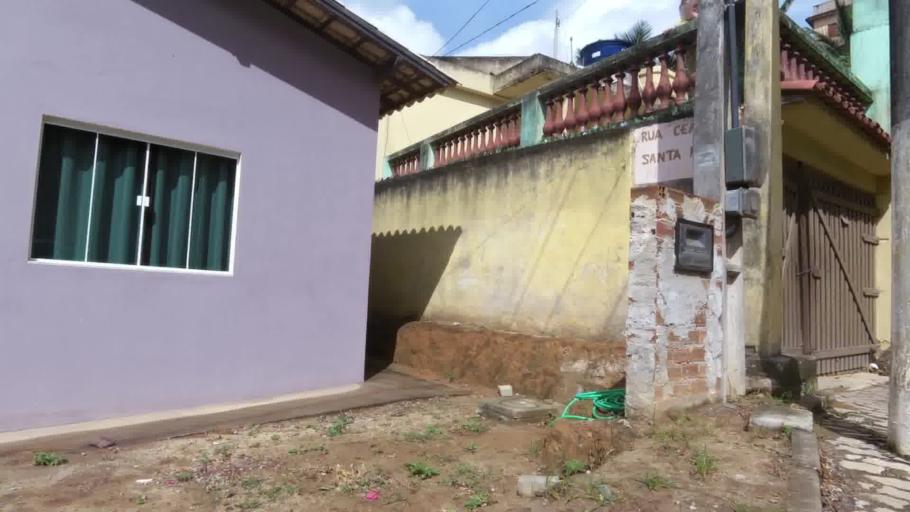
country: BR
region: Espirito Santo
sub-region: Marataizes
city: Marataizes
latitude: -21.0336
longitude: -40.8226
